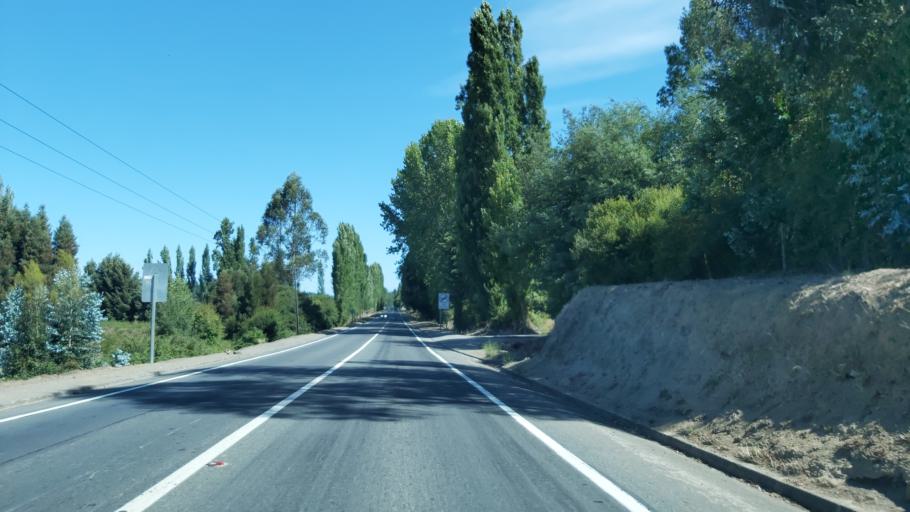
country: CL
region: Biobio
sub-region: Provincia de Concepcion
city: Lota
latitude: -37.1424
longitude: -72.9781
